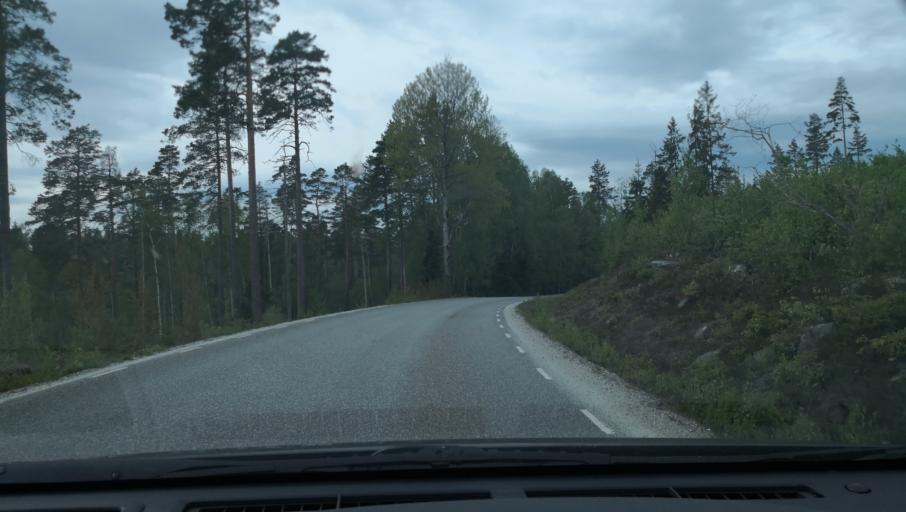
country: SE
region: Vaestmanland
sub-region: Skinnskattebergs Kommun
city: Skinnskatteberg
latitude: 59.8239
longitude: 15.5818
